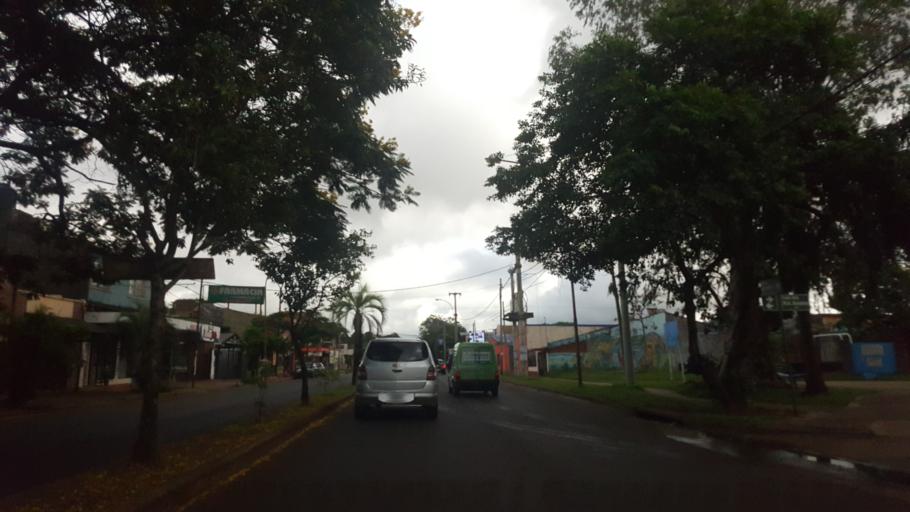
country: AR
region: Misiones
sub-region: Departamento de Capital
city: Posadas
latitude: -27.3700
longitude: -55.9169
